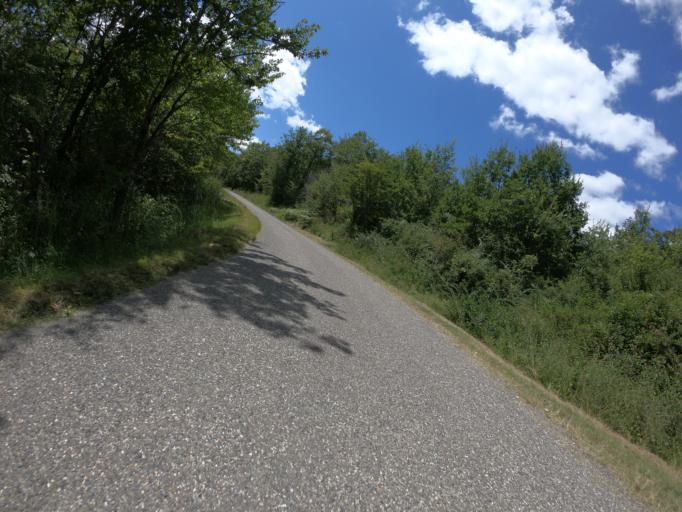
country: FR
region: Midi-Pyrenees
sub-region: Departement de l'Ariege
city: Mirepoix
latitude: 43.0553
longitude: 1.8363
